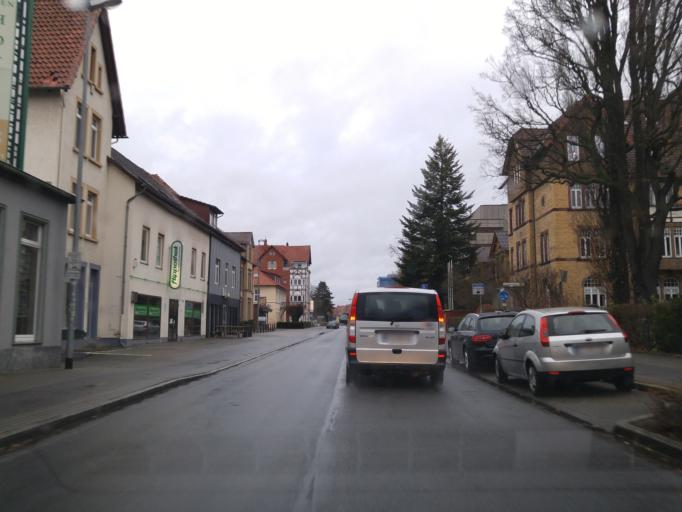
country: DE
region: Lower Saxony
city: Goettingen
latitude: 51.5269
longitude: 9.9393
